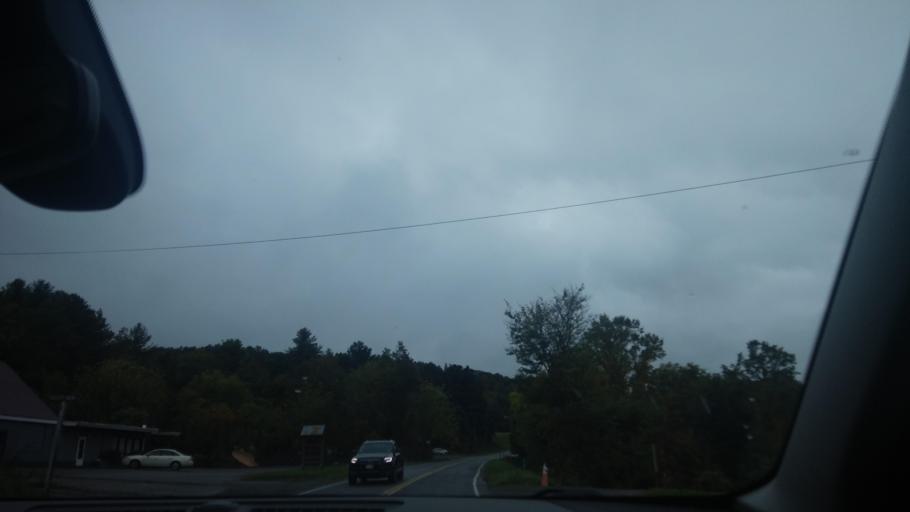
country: US
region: Virginia
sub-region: City of Galax
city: Galax
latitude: 36.6365
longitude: -80.9180
